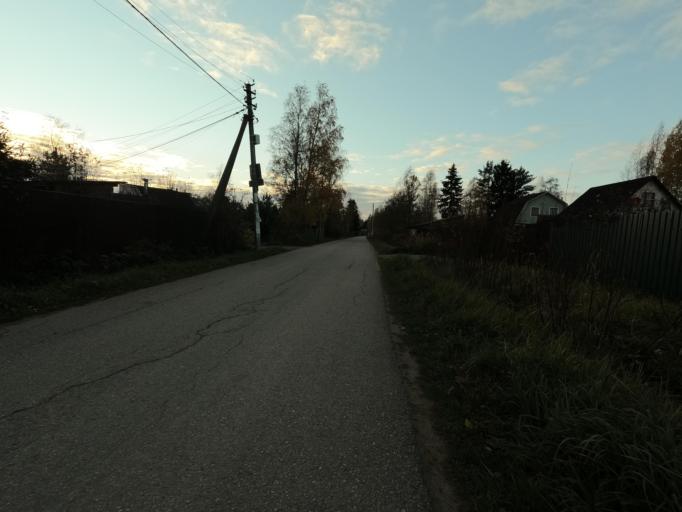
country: RU
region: Leningrad
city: Mga
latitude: 59.7761
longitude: 31.2095
